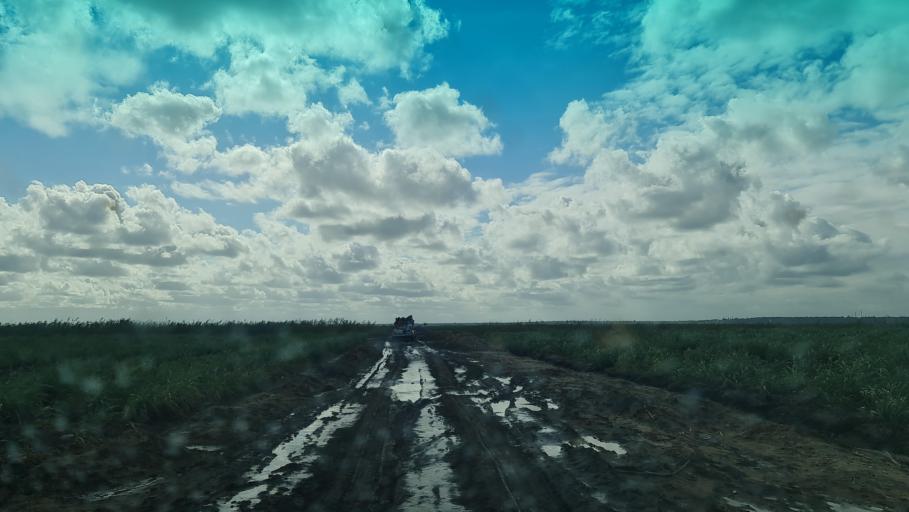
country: MZ
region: Maputo
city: Manhica
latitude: -25.4387
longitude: 32.8535
